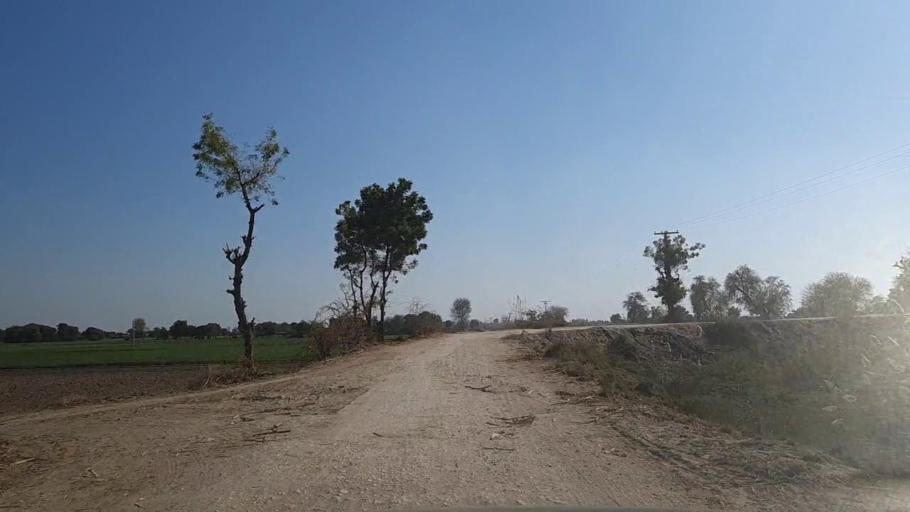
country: PK
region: Sindh
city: Nawabshah
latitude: 26.2252
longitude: 68.4289
